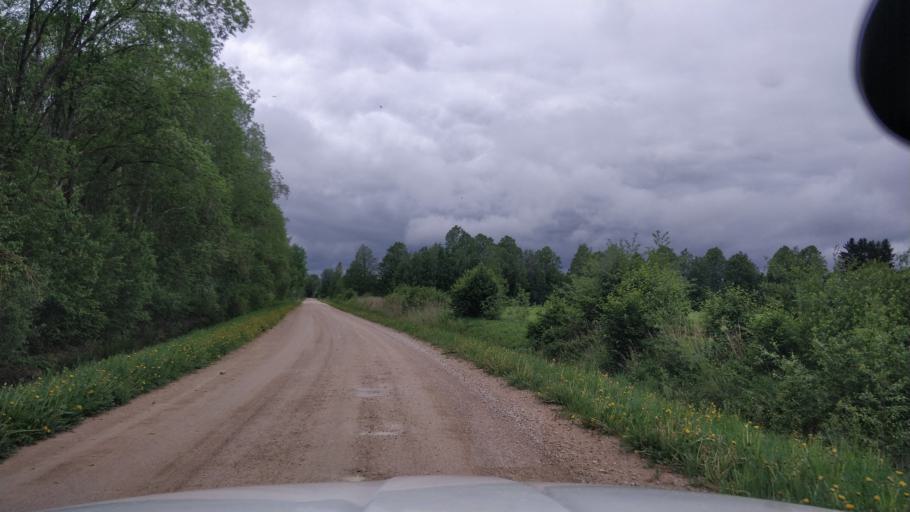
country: EE
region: Paernumaa
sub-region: Halinga vald
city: Parnu-Jaagupi
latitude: 58.7152
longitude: 24.3100
